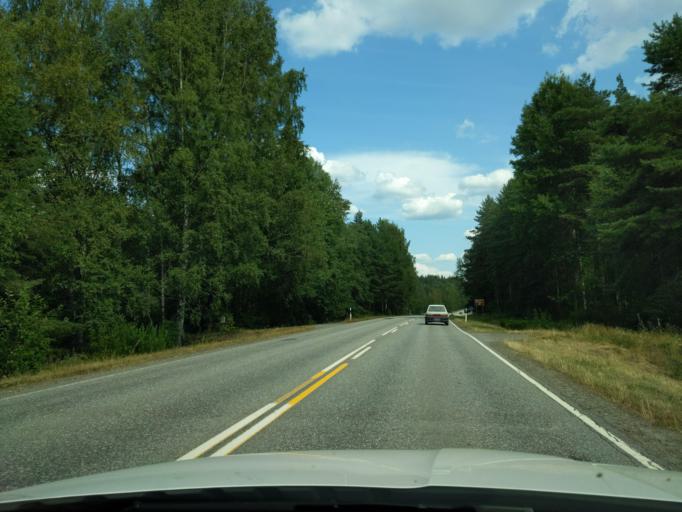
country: FI
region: Haeme
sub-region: Haemeenlinna
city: Lammi
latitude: 61.1281
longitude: 24.9608
